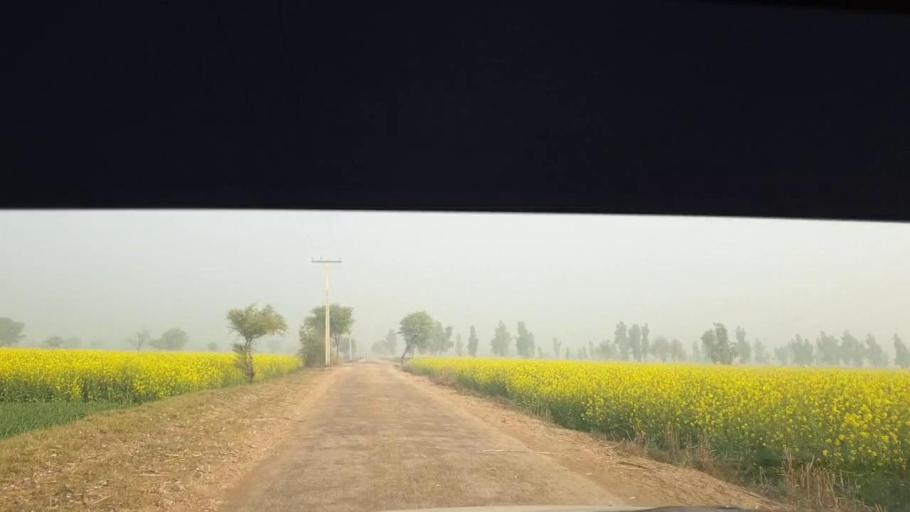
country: PK
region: Sindh
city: Berani
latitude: 25.7886
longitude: 68.7717
